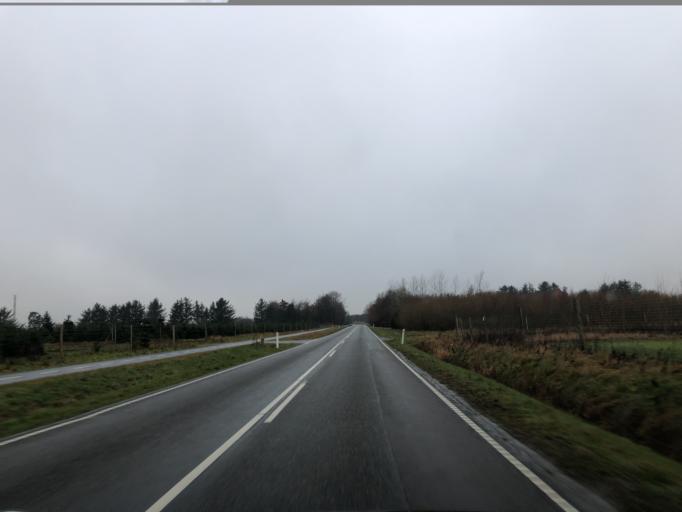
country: DK
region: Central Jutland
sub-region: Holstebro Kommune
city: Ulfborg
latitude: 56.1942
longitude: 8.3264
